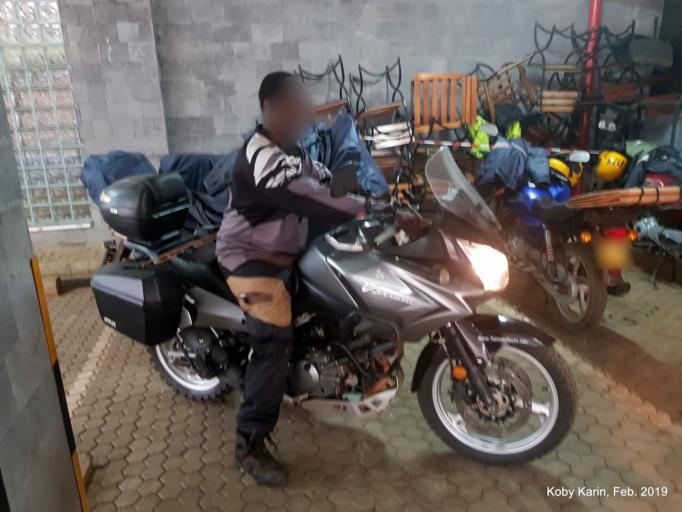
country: KE
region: Nairobi Area
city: Nairobi
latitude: -1.2642
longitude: 36.7969
